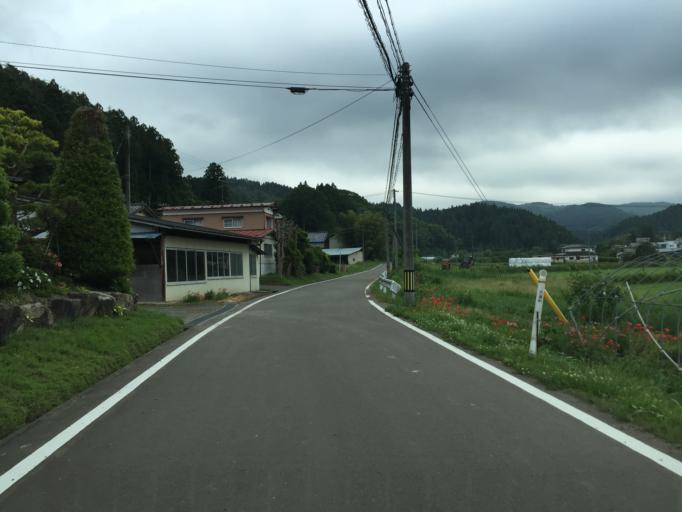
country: JP
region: Miyagi
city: Marumori
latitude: 37.8326
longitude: 140.7307
